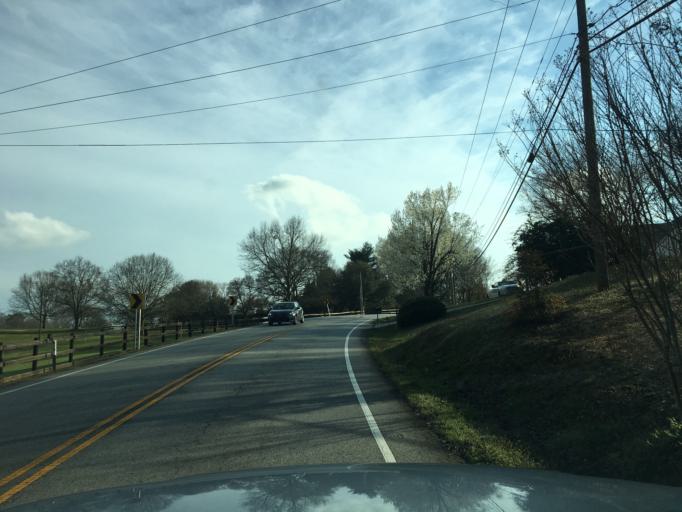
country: US
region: South Carolina
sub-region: Greenville County
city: Taylors
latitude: 34.8812
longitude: -82.2911
